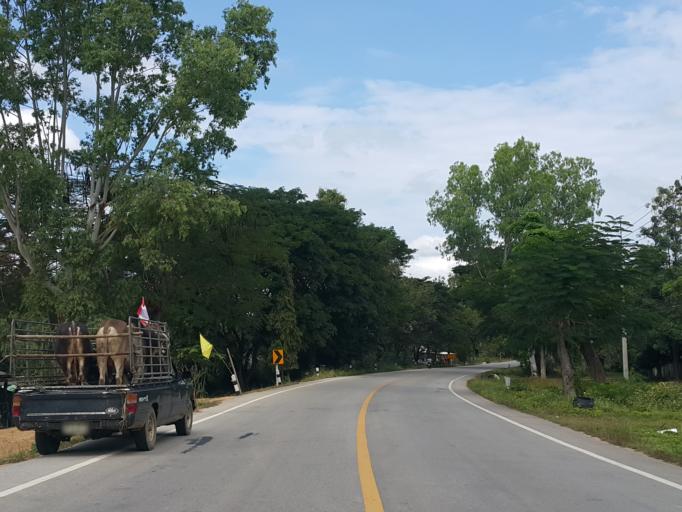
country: TH
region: Lampang
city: Hang Chat
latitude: 18.4262
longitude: 99.4437
